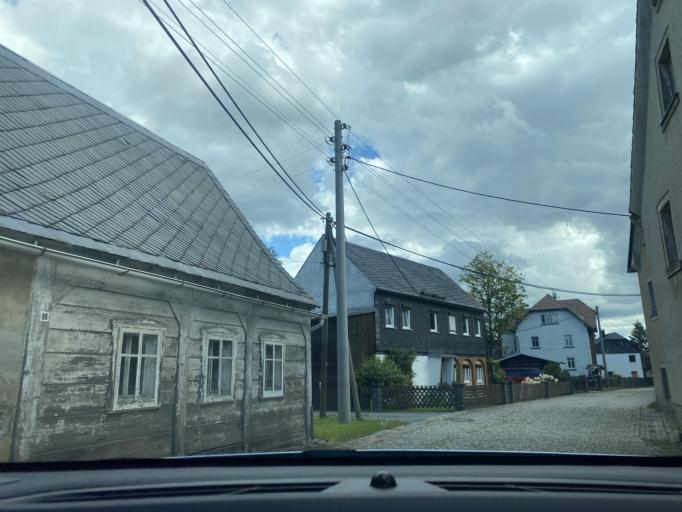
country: DE
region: Saxony
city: Schonbach
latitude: 51.0624
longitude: 14.5714
